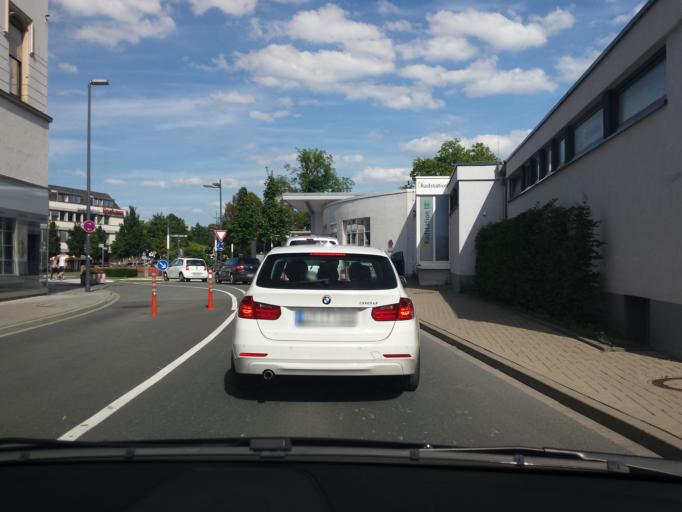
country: DE
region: North Rhine-Westphalia
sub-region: Regierungsbezirk Arnsberg
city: Lippstadt
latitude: 51.6709
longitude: 8.3479
